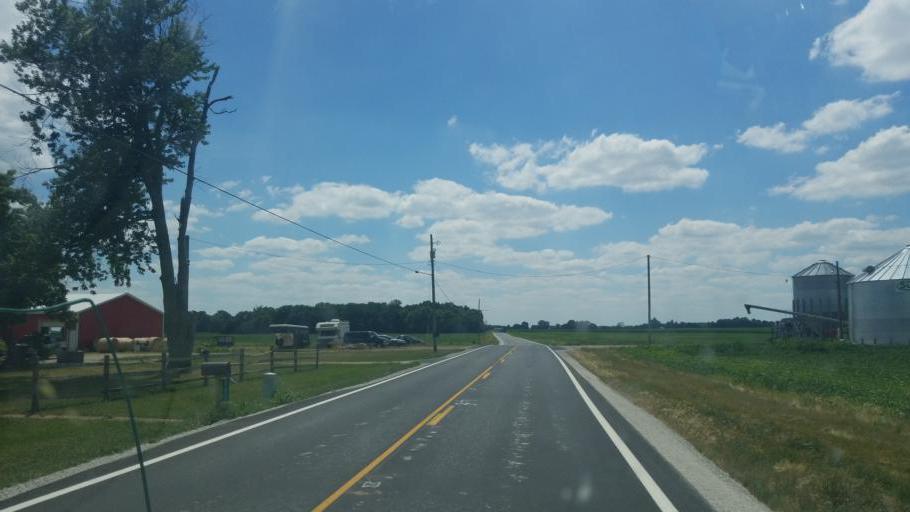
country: US
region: Ohio
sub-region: Defiance County
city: Hicksville
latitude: 41.3348
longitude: -84.6943
